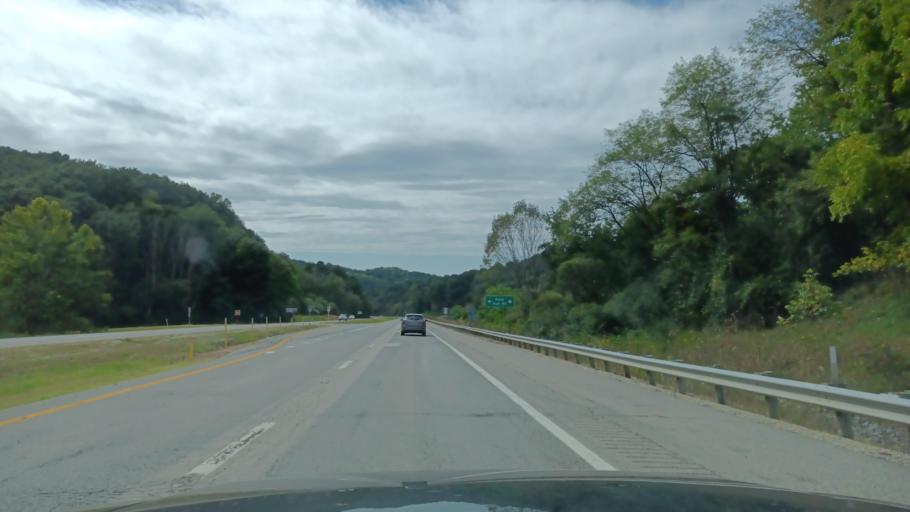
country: US
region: West Virginia
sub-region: Ritchie County
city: Harrisville
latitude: 39.2594
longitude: -81.1669
